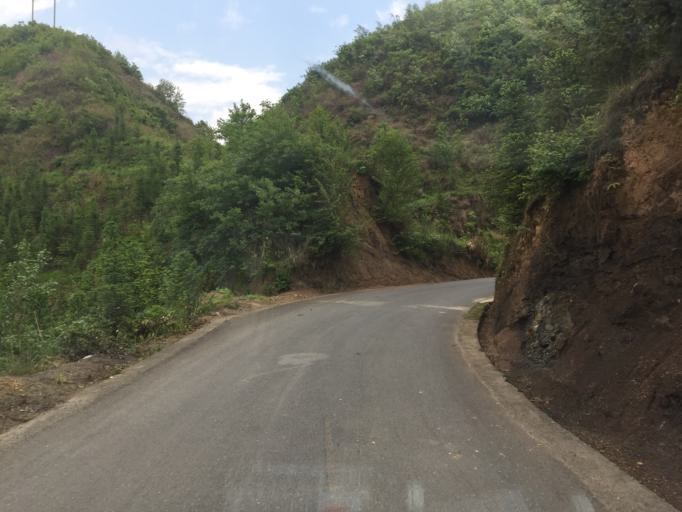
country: CN
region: Guangxi Zhuangzu Zizhiqu
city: Xinzhou
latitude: 25.6580
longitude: 105.2342
